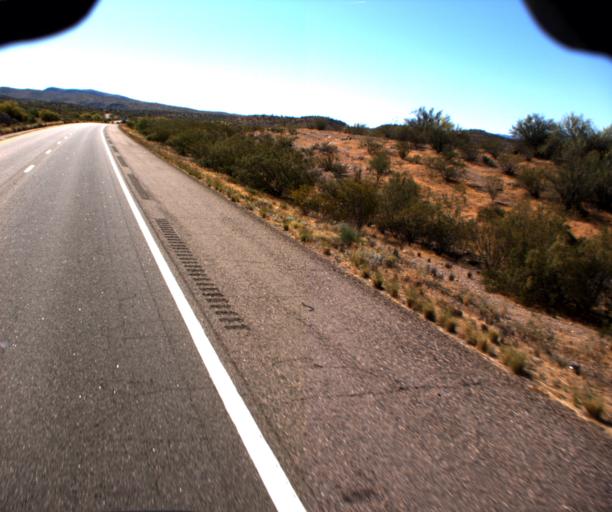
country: US
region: Arizona
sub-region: Yavapai County
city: Bagdad
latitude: 34.6293
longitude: -113.5422
